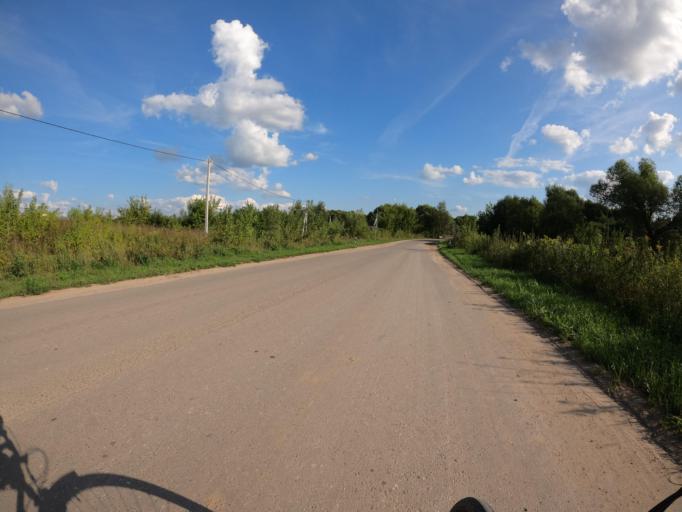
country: RU
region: Moskovskaya
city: Troitskoye
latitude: 55.1948
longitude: 38.4895
